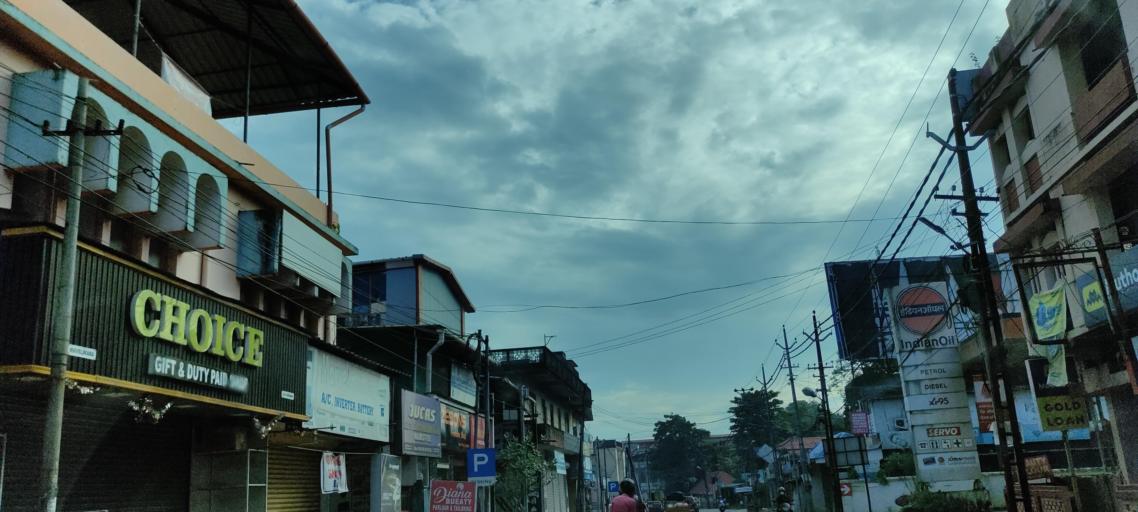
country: IN
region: Kerala
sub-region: Alappuzha
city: Mavelikara
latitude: 9.2531
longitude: 76.5439
